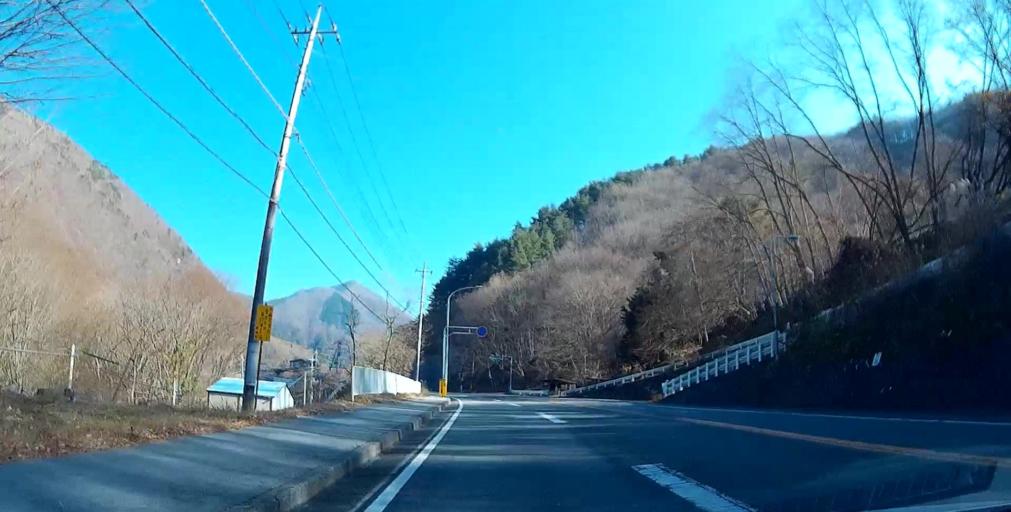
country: JP
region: Yamanashi
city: Fujikawaguchiko
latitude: 35.5868
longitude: 138.7398
